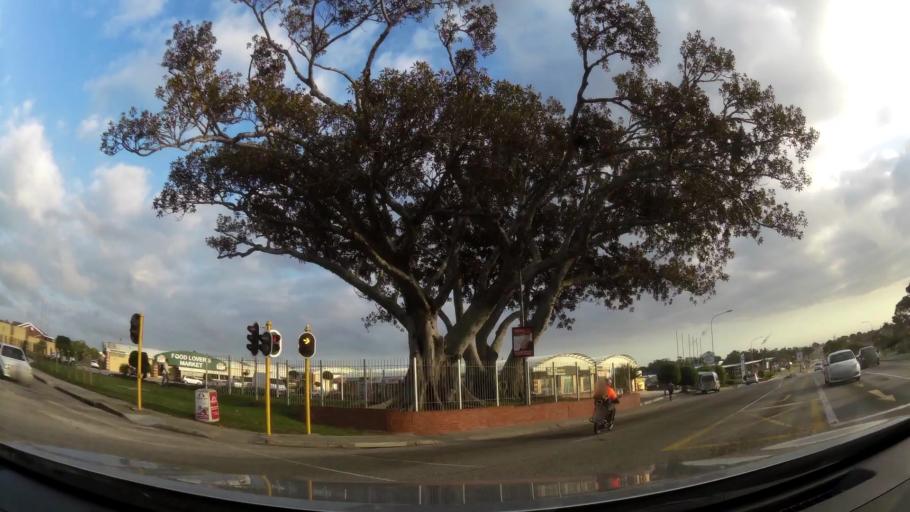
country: ZA
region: Eastern Cape
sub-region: Nelson Mandela Bay Metropolitan Municipality
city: Port Elizabeth
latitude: -33.9815
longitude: 25.5532
